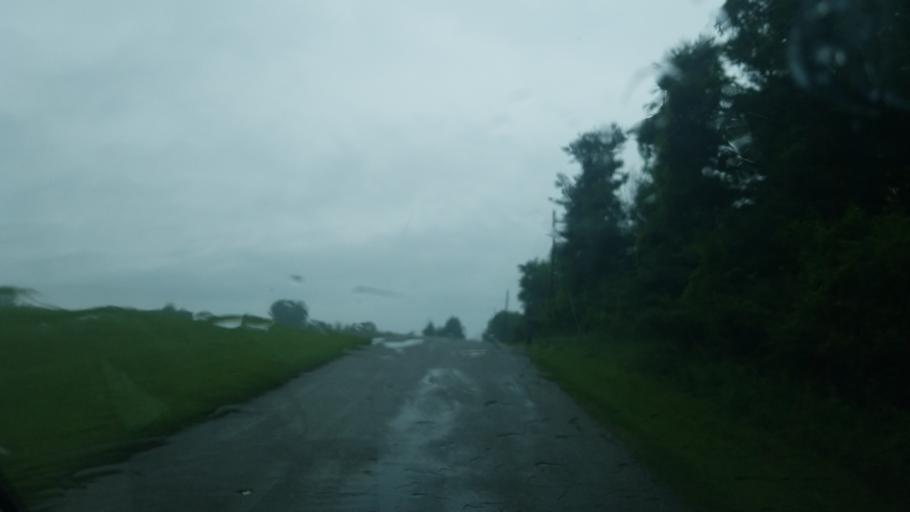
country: US
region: Ohio
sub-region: Richland County
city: Shelby
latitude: 40.9280
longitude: -82.7976
